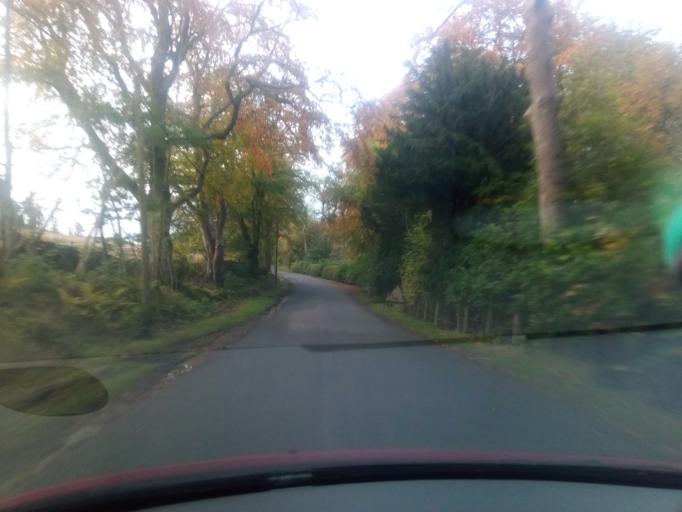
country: GB
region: Scotland
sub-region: The Scottish Borders
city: Jedburgh
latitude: 55.3742
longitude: -2.6475
